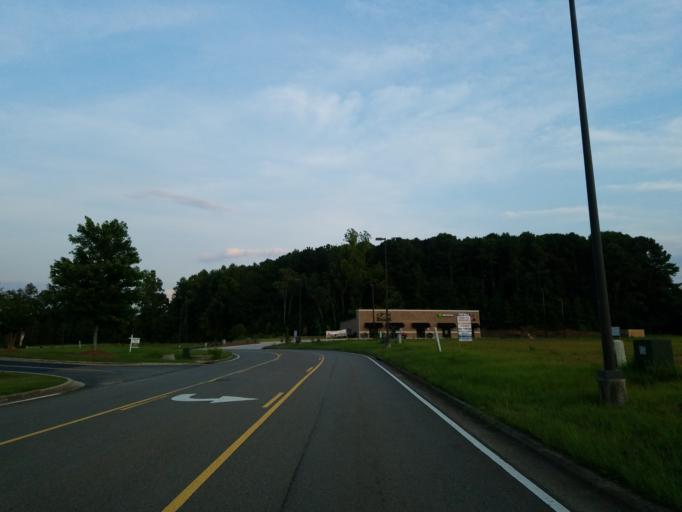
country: US
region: Georgia
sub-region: Pickens County
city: Jasper
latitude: 34.4694
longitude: -84.4589
